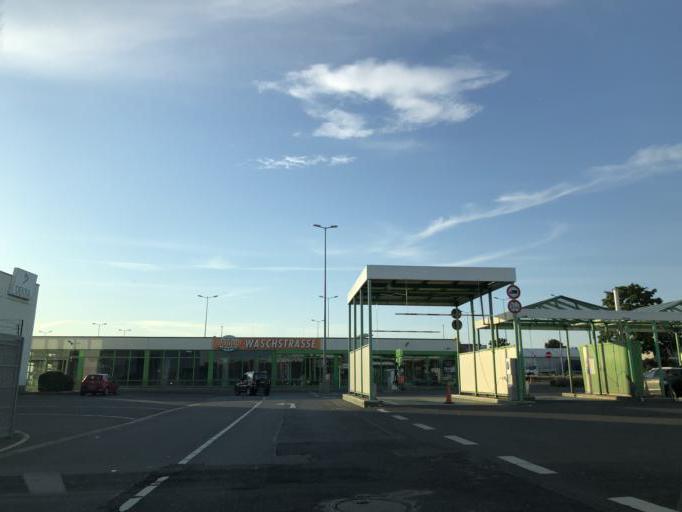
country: DE
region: Rheinland-Pfalz
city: Gensingen
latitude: 49.9027
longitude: 7.9308
